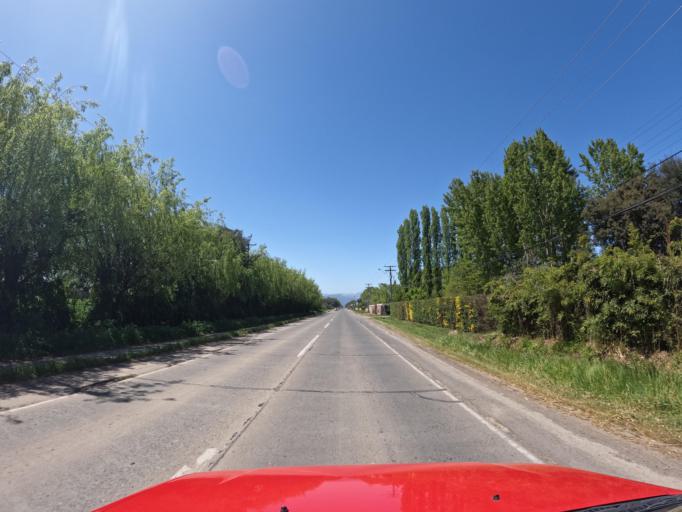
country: CL
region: Maule
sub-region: Provincia de Linares
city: Linares
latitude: -35.8334
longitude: -71.5376
